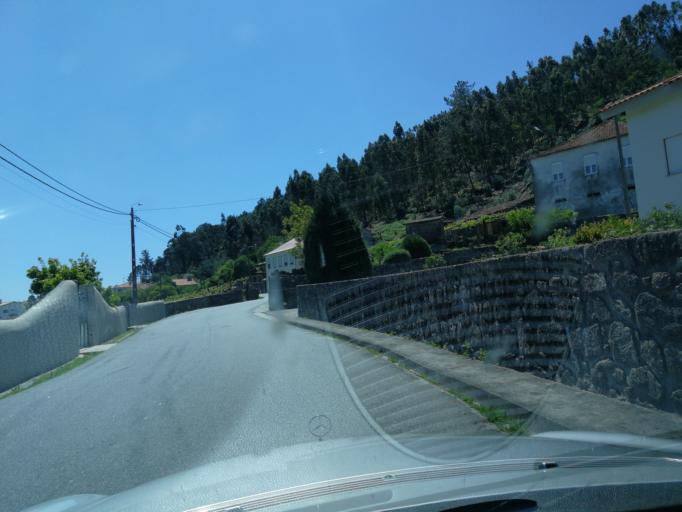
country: PT
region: Viana do Castelo
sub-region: Viana do Castelo
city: Meadela
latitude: 41.7431
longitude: -8.7824
